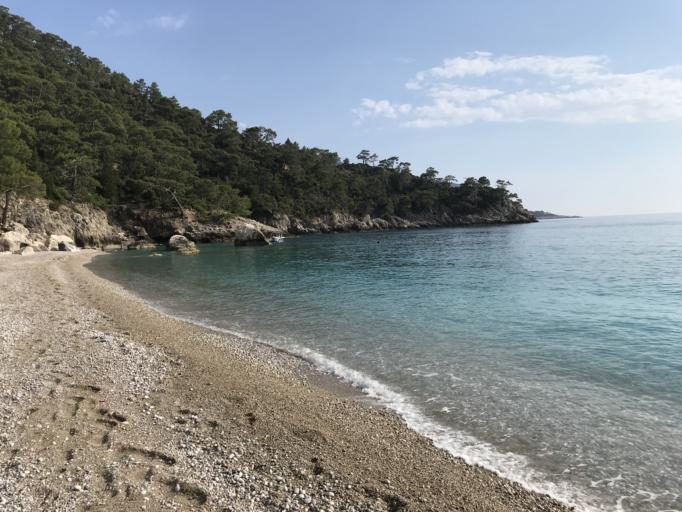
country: TR
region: Mugla
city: OEluedeniz
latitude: 36.4407
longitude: 29.1313
